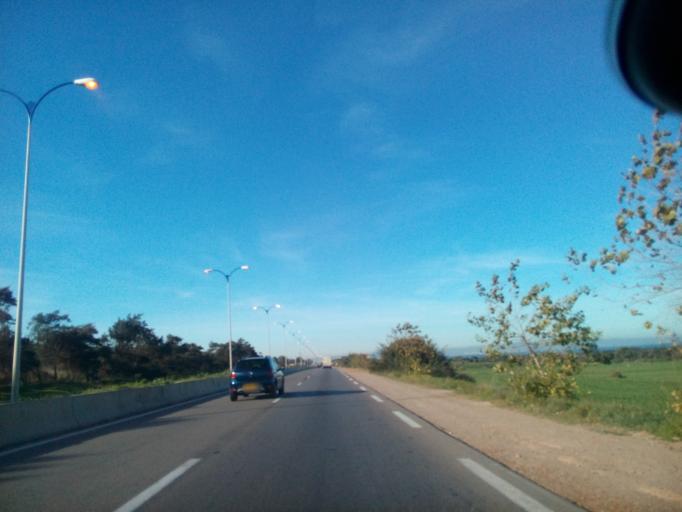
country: DZ
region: Mostaganem
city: Mostaganem
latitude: 35.8039
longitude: -0.0581
